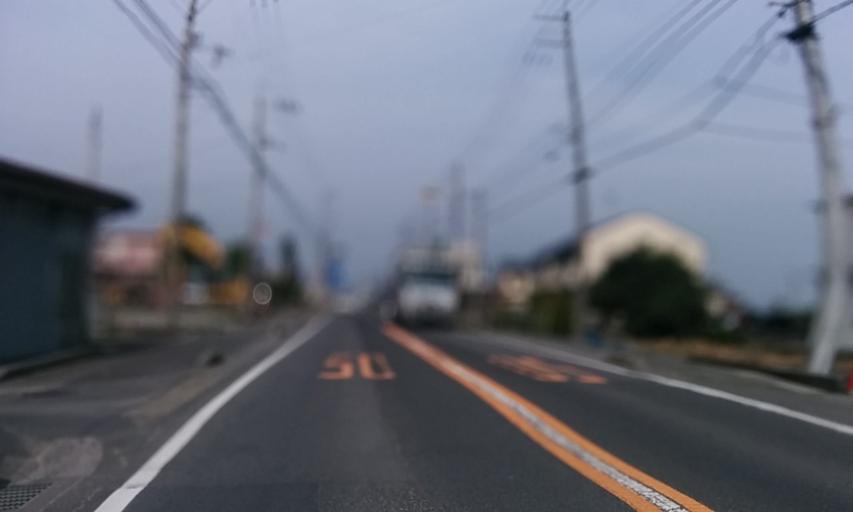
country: JP
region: Ehime
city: Kawanoecho
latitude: 33.9675
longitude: 133.4806
